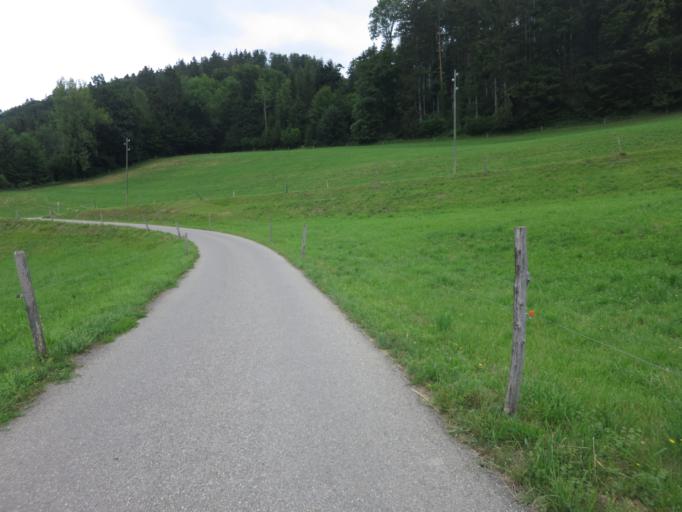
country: CH
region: Saint Gallen
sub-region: Wahlkreis Toggenburg
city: Buetschwil
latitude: 47.3677
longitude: 9.0840
